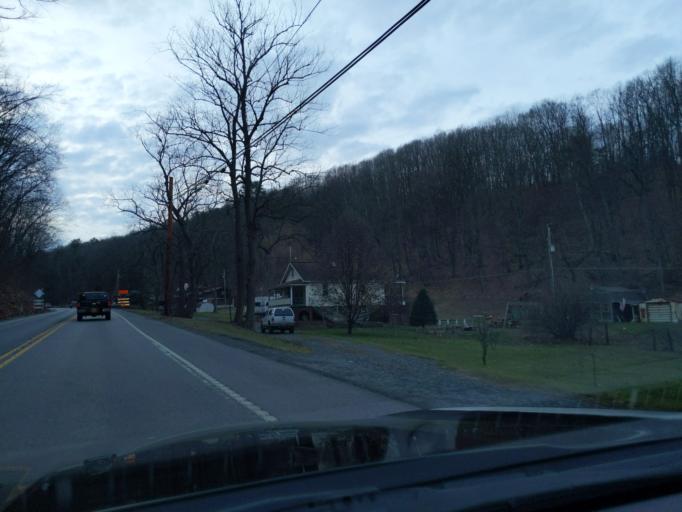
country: US
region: Pennsylvania
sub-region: Blair County
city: Williamsburg
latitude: 40.4712
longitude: -78.2858
